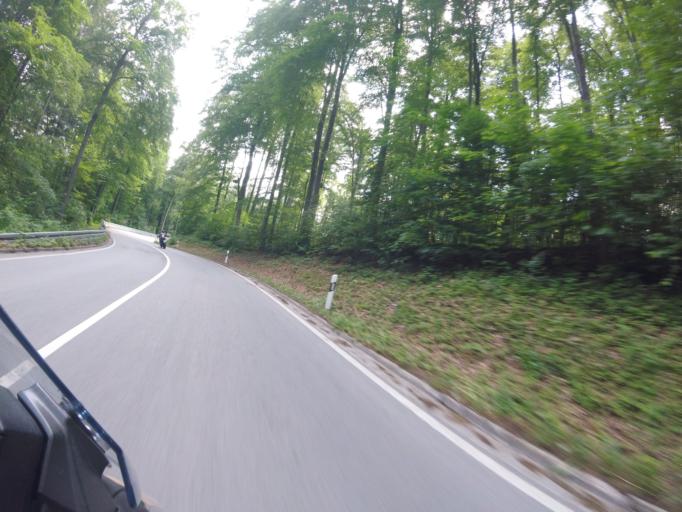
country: DE
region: Bavaria
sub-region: Upper Bavaria
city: Schaftlarn
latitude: 47.9870
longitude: 11.4620
